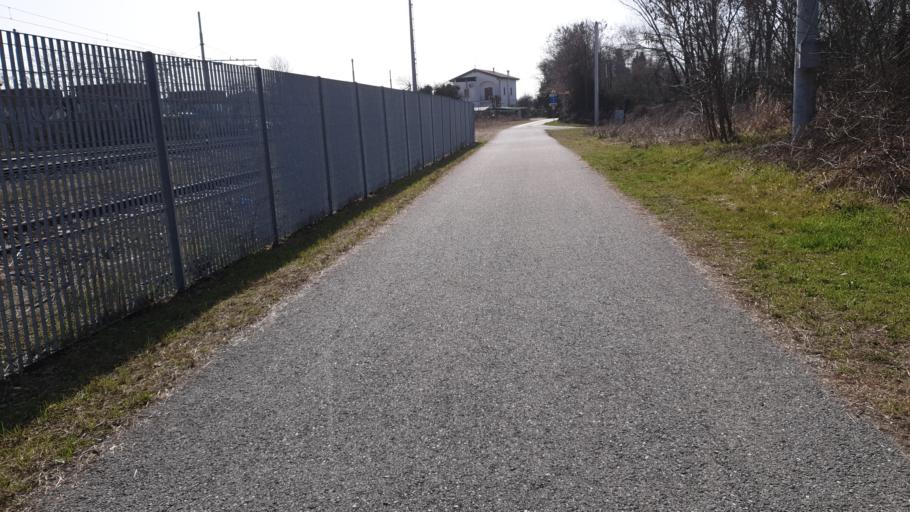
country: IT
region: Veneto
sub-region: Provincia di Padova
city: Camposampiero
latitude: 45.5643
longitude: 11.9261
